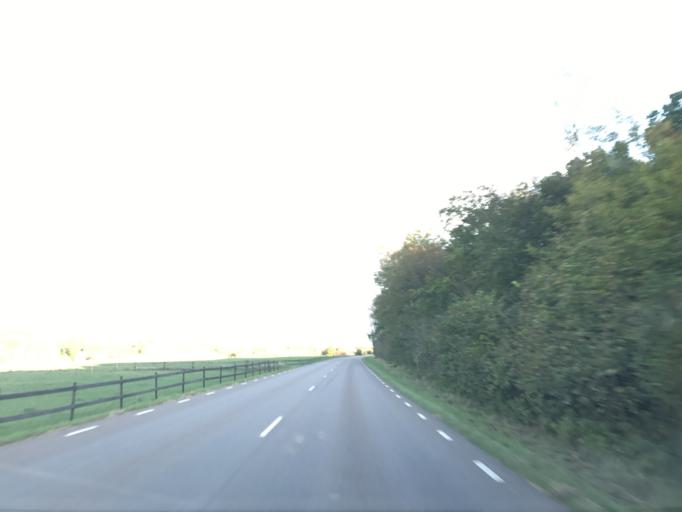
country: SE
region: Skane
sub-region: Klippans Kommun
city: Ljungbyhed
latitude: 56.1418
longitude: 13.2678
